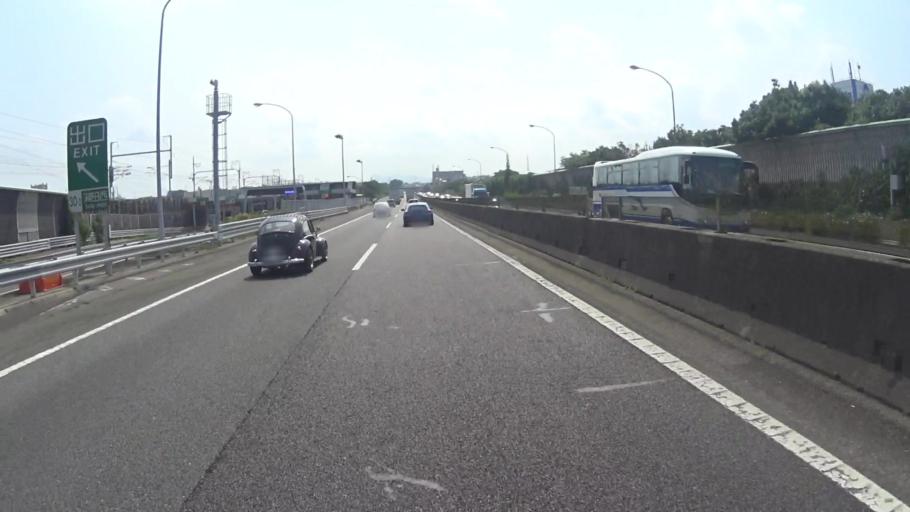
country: JP
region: Shiga Prefecture
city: Otsu-shi
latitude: 34.9692
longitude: 135.9081
